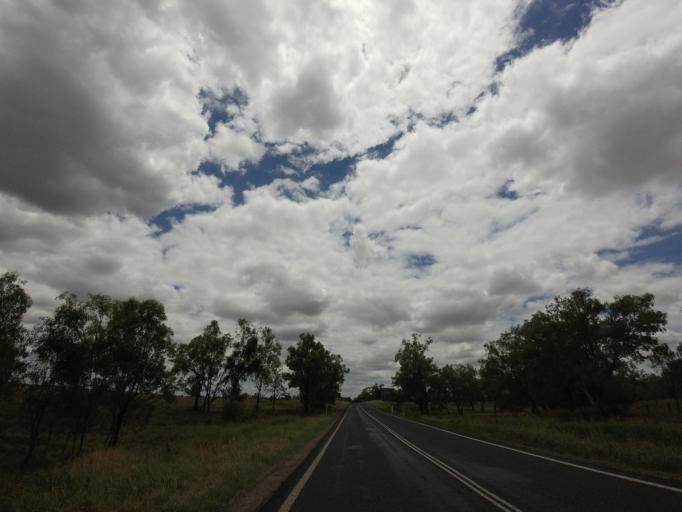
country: AU
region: Queensland
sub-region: Goondiwindi
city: Goondiwindi
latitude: -28.5051
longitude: 150.2908
